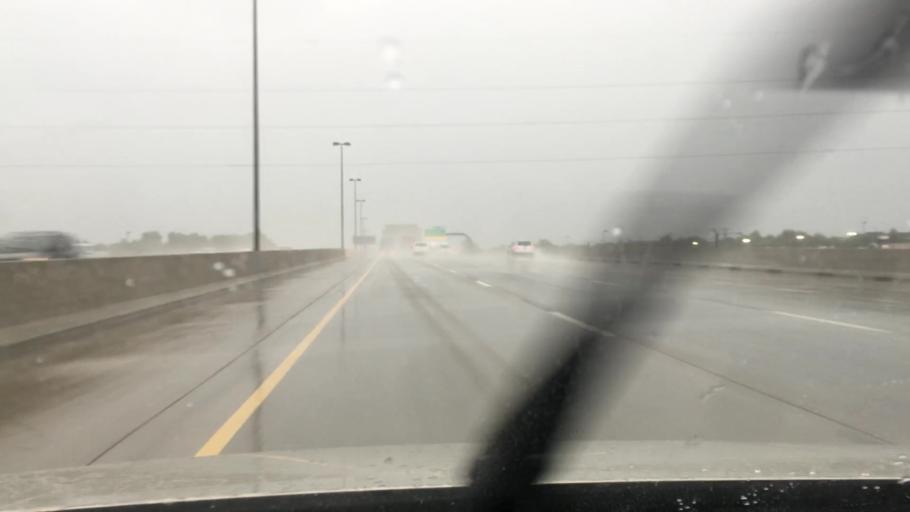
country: US
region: Oklahoma
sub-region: Tulsa County
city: Jenks
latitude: 36.0904
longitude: -95.9419
